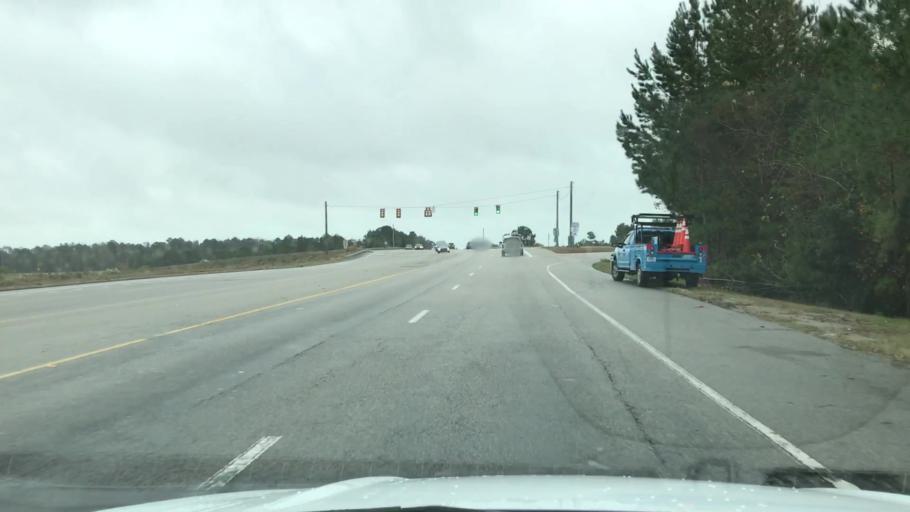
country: US
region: South Carolina
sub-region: Horry County
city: Myrtle Beach
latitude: 33.7570
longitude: -78.8558
